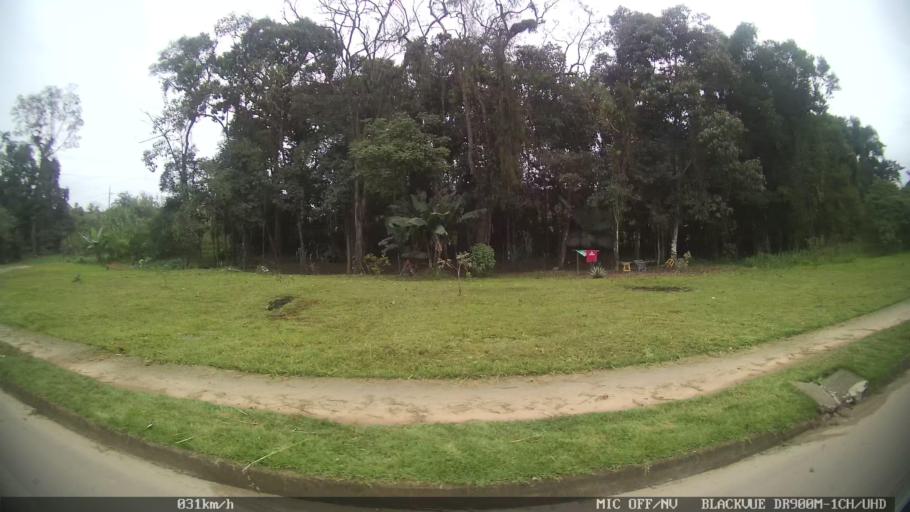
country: BR
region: Santa Catarina
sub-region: Joinville
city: Joinville
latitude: -26.2729
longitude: -48.8911
